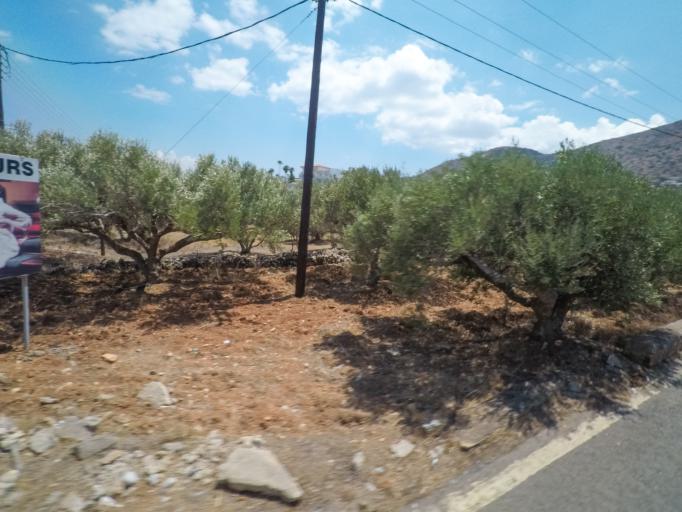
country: GR
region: Crete
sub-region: Nomos Lasithiou
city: Skhisma
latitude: 35.2480
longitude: 25.7286
